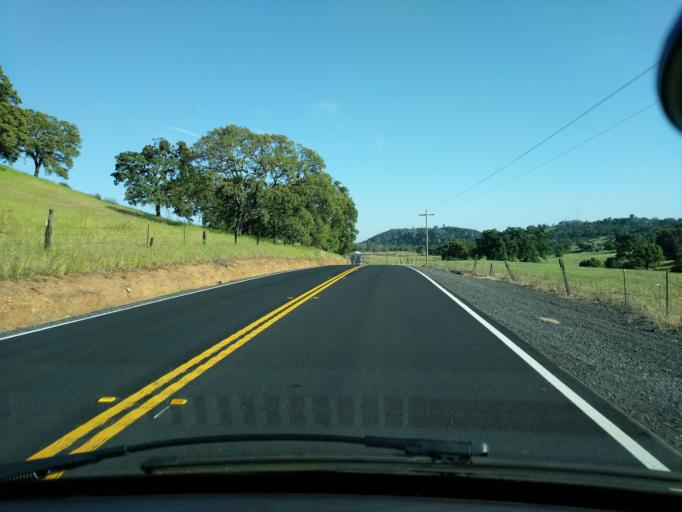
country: US
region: California
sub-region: Calaveras County
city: Copperopolis
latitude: 38.0250
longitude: -120.6452
